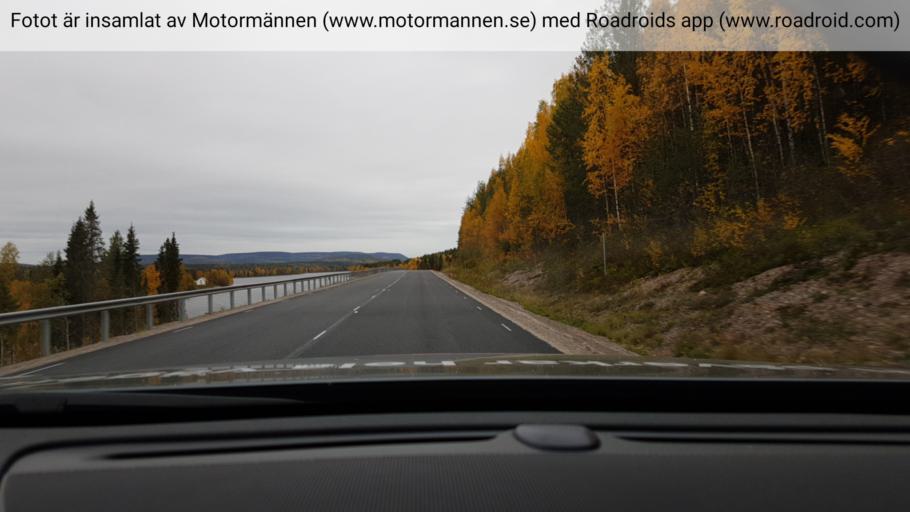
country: SE
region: Norrbotten
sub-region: Overkalix Kommun
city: OEverkalix
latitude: 66.4769
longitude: 22.7885
